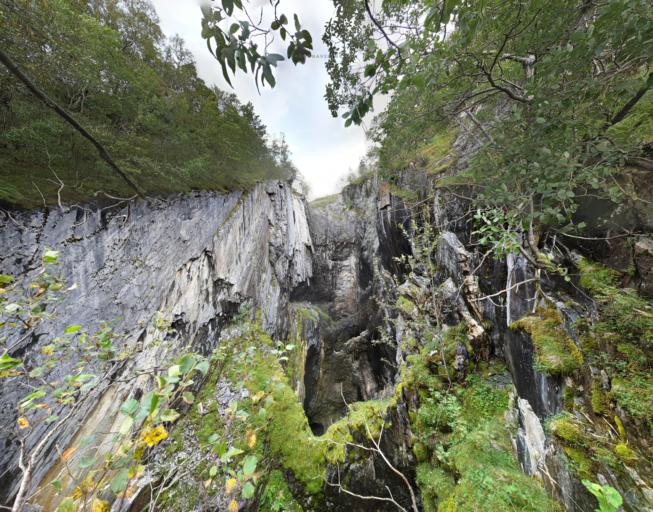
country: NO
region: Hordaland
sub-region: Bergen
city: Indre Arna
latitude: 60.4198
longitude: 5.6053
